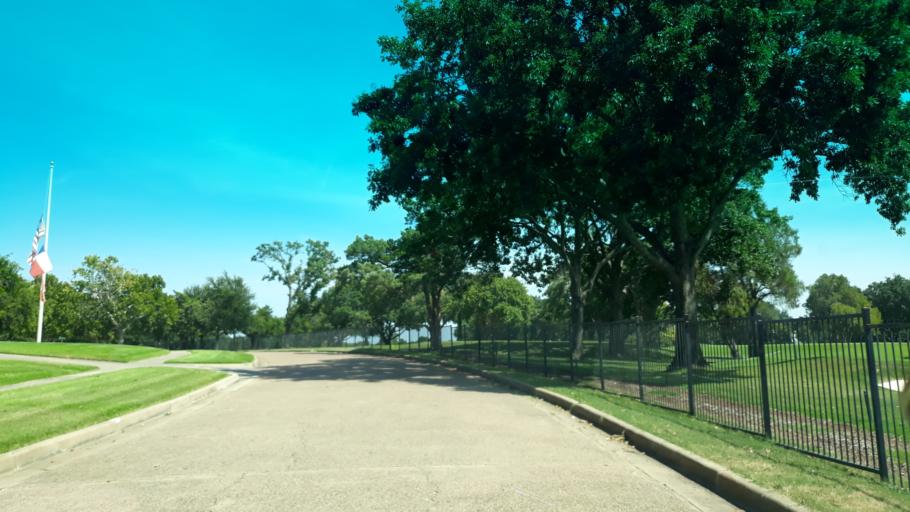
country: US
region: Texas
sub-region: Dallas County
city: Highland Park
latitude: 32.8153
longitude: -96.7482
